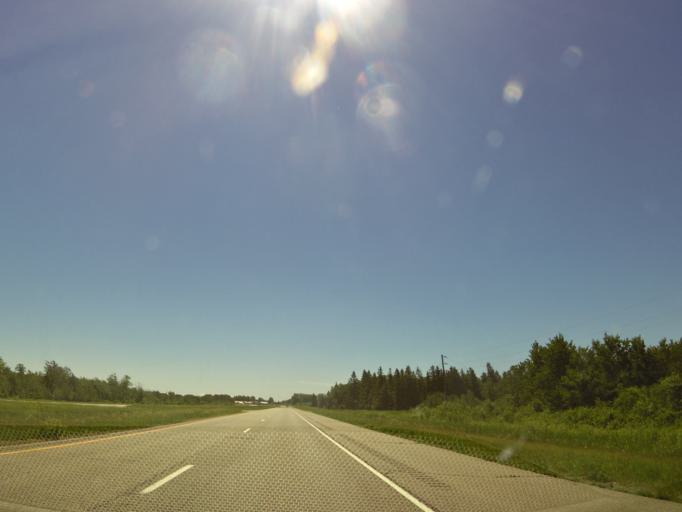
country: US
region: Minnesota
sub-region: Red Lake County
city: Red Lake Falls
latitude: 47.7082
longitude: -96.1602
